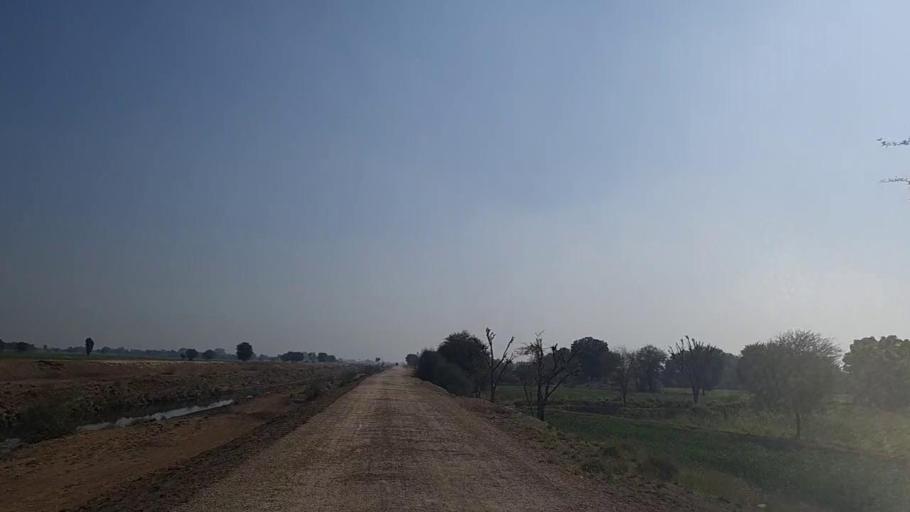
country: PK
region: Sindh
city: Shahpur Chakar
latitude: 26.1840
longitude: 68.5643
